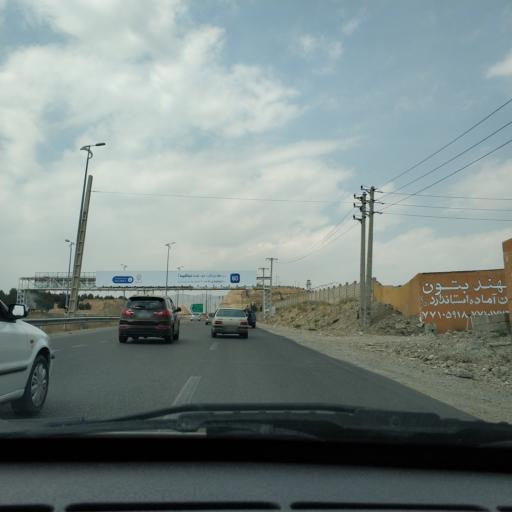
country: IR
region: Tehran
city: Tajrish
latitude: 35.7840
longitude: 51.5652
